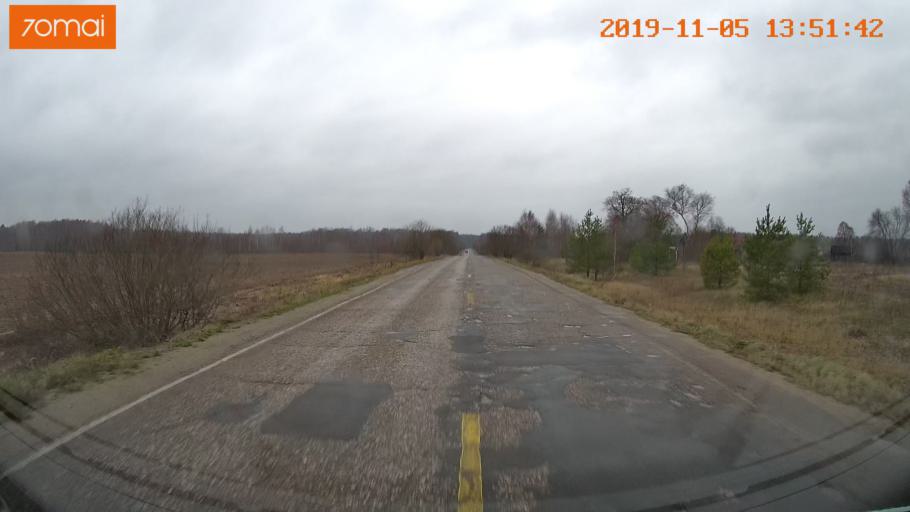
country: RU
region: Ivanovo
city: Kaminskiy
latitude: 57.0255
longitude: 41.3974
